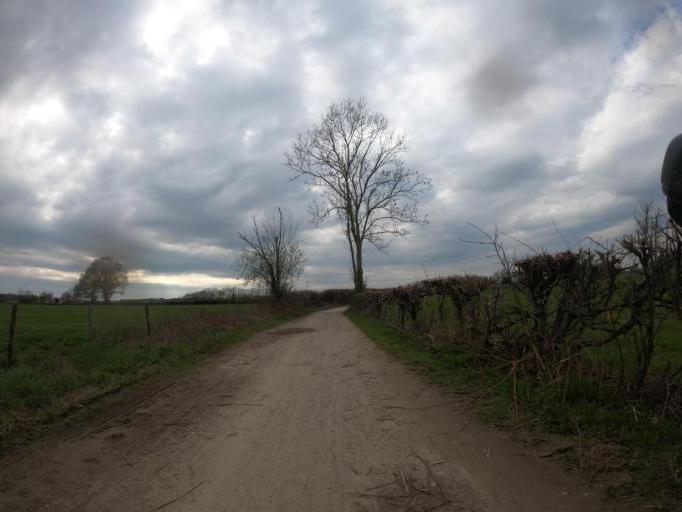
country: DE
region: North Rhine-Westphalia
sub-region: Regierungsbezirk Koln
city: Aachen
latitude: 50.7382
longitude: 6.1358
